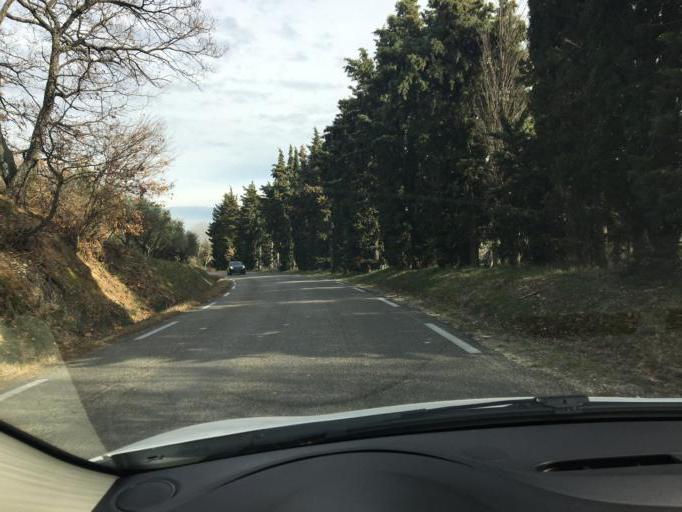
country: FR
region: Provence-Alpes-Cote d'Azur
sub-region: Departement du Vaucluse
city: Saignon
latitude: 43.9195
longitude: 5.4825
